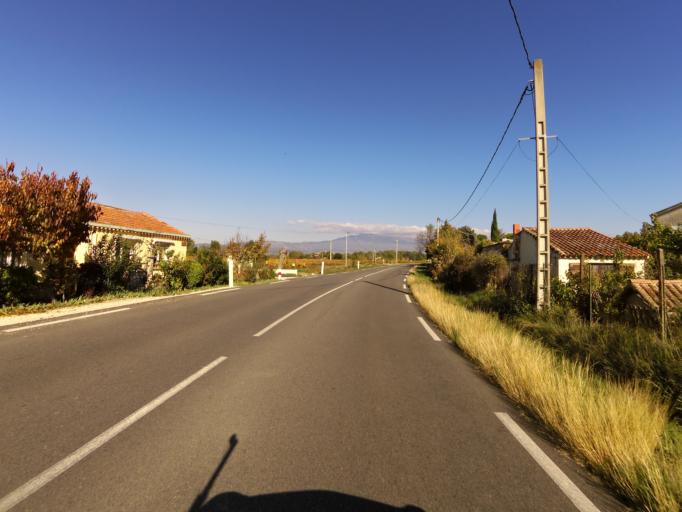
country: FR
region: Provence-Alpes-Cote d'Azur
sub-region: Departement du Vaucluse
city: Caromb
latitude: 44.0744
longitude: 5.0880
